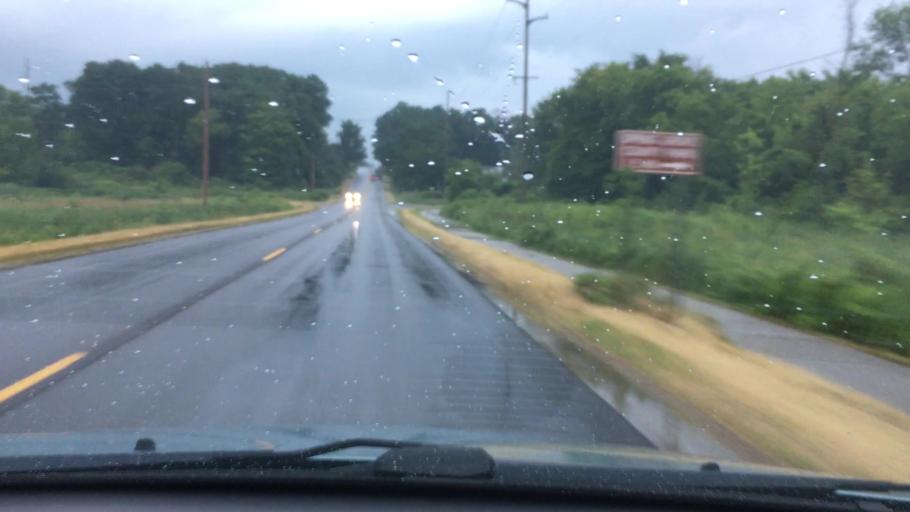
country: US
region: Michigan
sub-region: Ottawa County
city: Hudsonville
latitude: 42.8346
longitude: -85.8024
